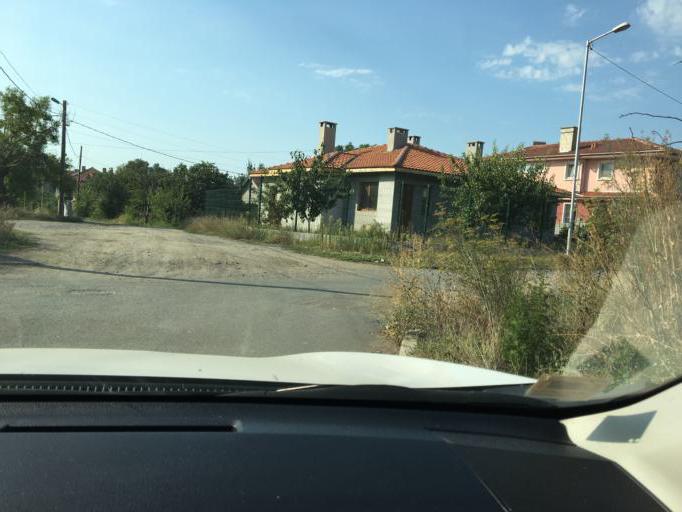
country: BG
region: Burgas
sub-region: Obshtina Burgas
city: Burgas
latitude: 42.6128
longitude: 27.4851
